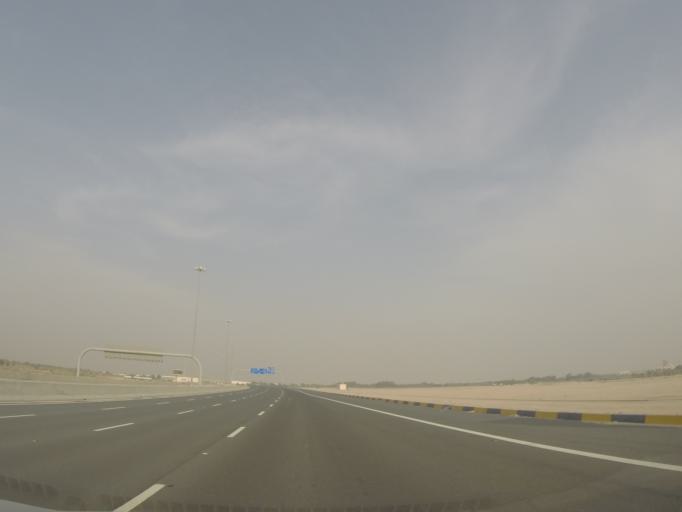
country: AE
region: Abu Dhabi
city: Abu Dhabi
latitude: 24.6991
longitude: 54.7627
